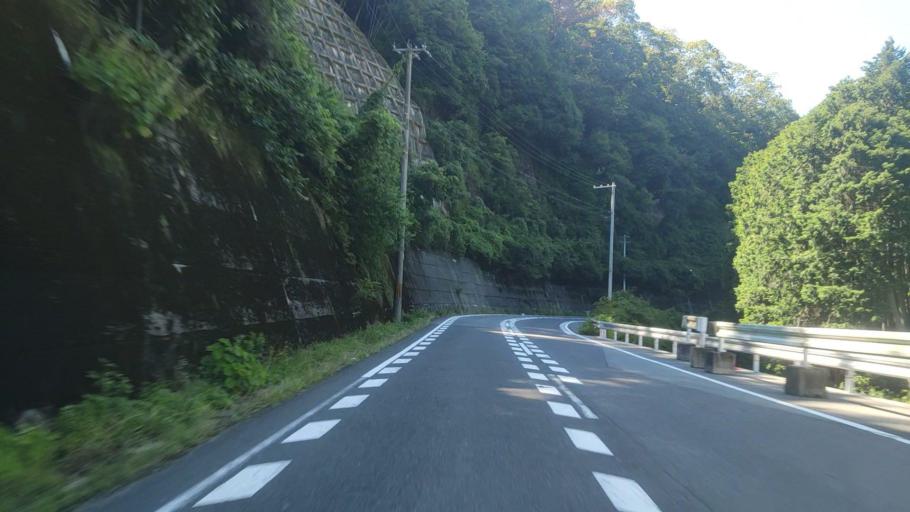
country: JP
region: Nara
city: Yoshino-cho
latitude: 34.4286
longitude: 135.9380
